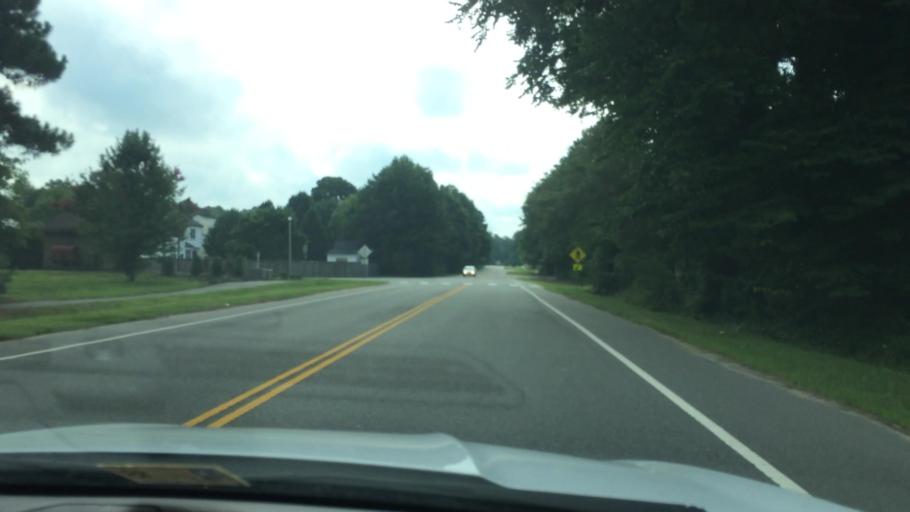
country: US
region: Virginia
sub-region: City of Poquoson
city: Poquoson
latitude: 37.1049
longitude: -76.4547
